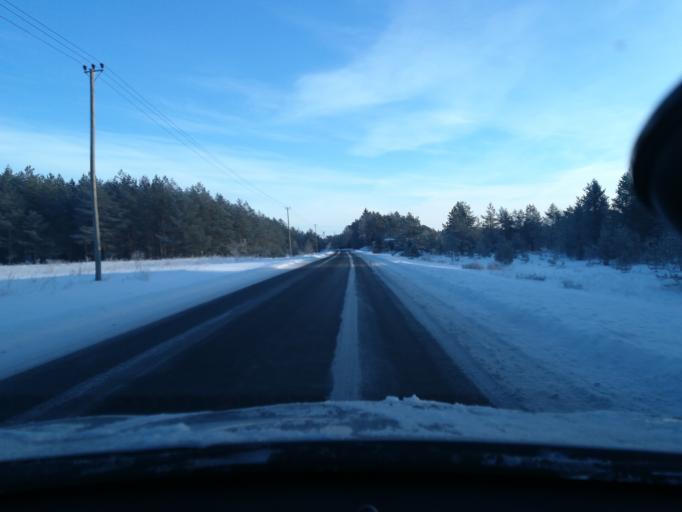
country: EE
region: Harju
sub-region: Keila linn
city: Keila
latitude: 59.3828
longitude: 24.4378
